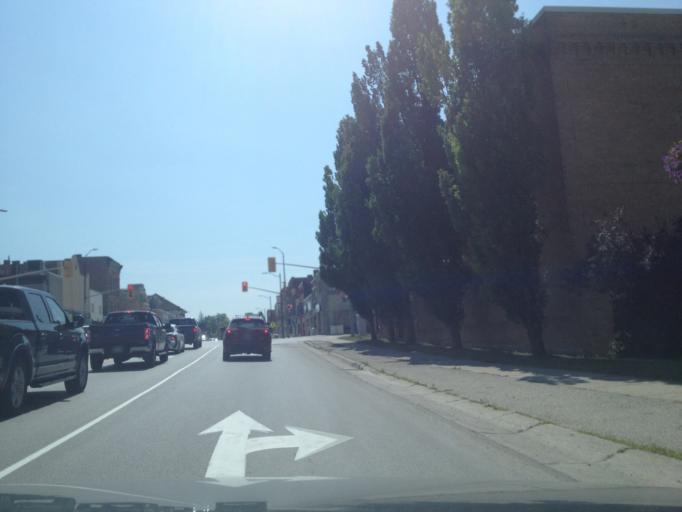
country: CA
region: Ontario
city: Huron East
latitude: 43.4684
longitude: -81.1987
